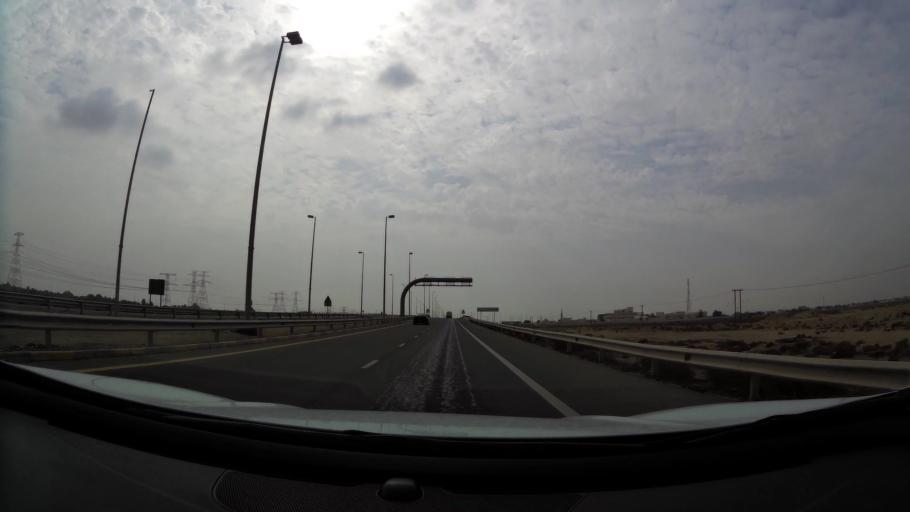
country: AE
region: Abu Dhabi
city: Abu Dhabi
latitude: 24.6634
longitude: 54.7421
